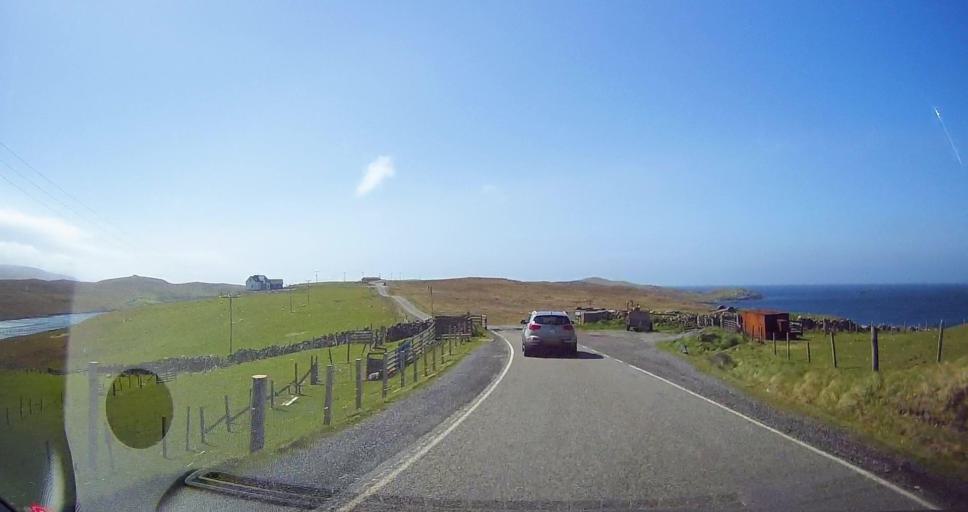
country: GB
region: Scotland
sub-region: Shetland Islands
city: Sandwick
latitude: 60.0950
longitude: -1.3217
